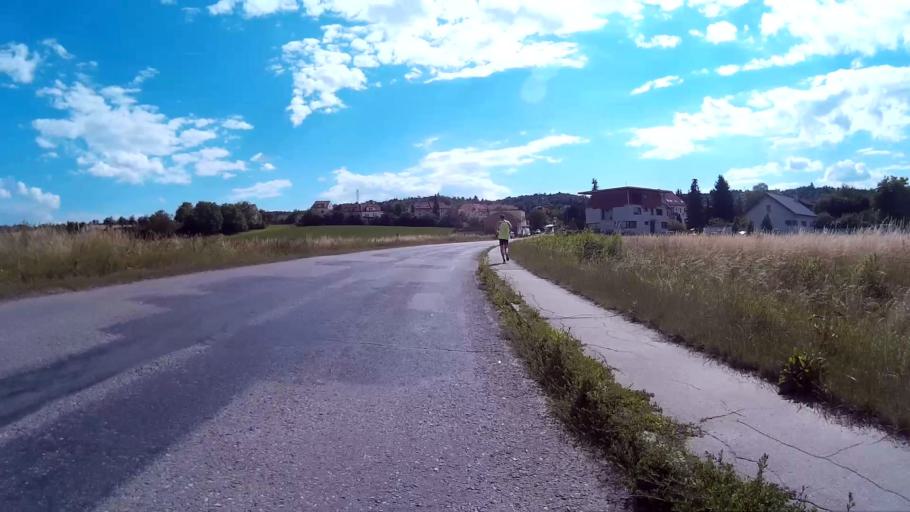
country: CZ
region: South Moravian
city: Ostopovice
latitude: 49.1608
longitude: 16.5527
